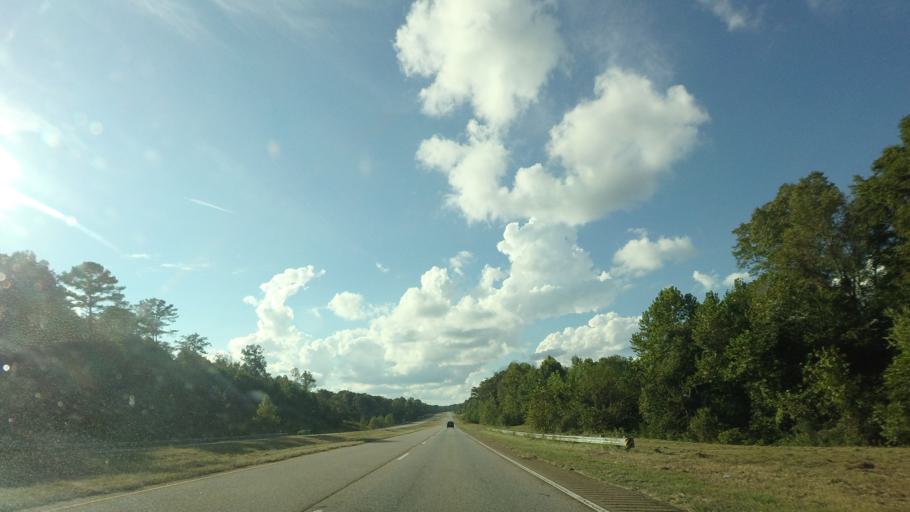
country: US
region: Georgia
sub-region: Pulaski County
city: Hawkinsville
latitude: 32.3620
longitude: -83.6007
